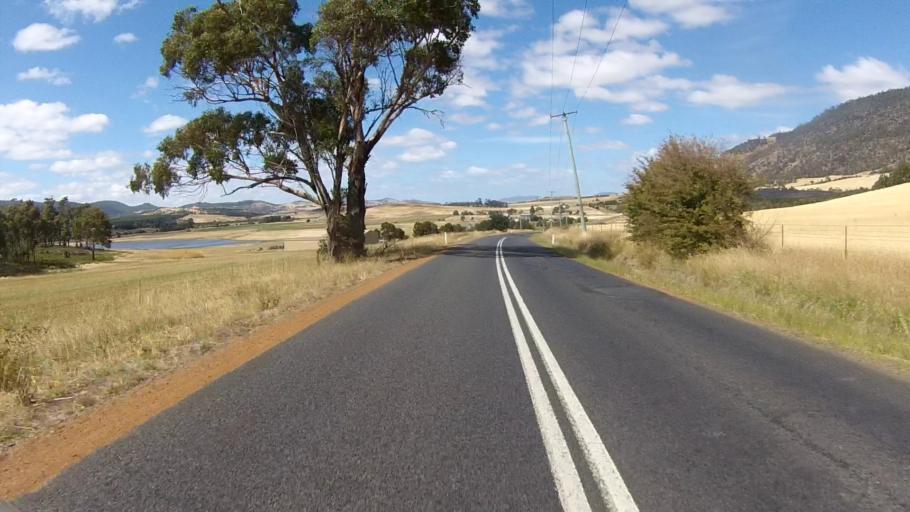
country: AU
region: Tasmania
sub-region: Sorell
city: Sorell
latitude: -42.6189
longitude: 147.4297
